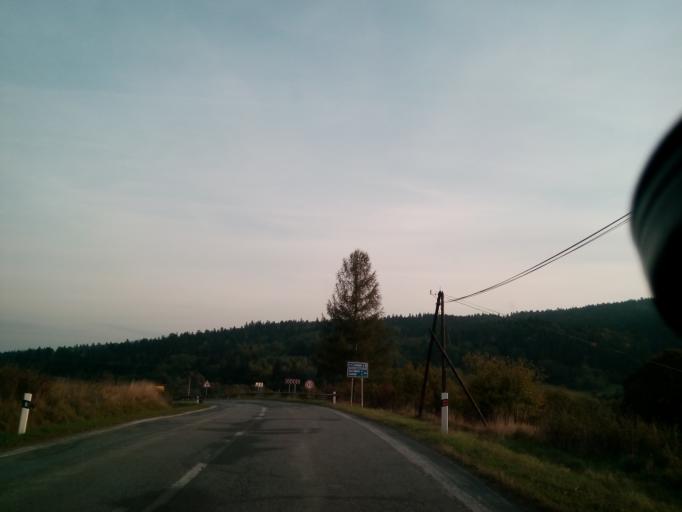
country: SK
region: Presovsky
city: Svidnik
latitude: 49.3566
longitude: 21.4770
